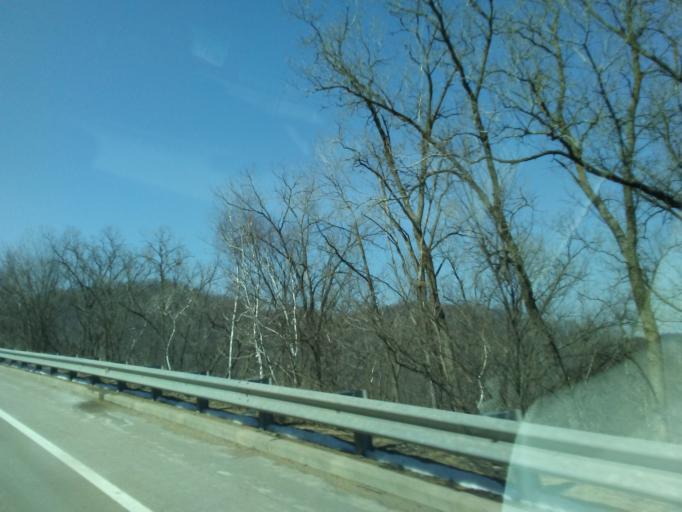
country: US
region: Wisconsin
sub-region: La Crosse County
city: West Salem
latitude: 43.7081
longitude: -91.0521
